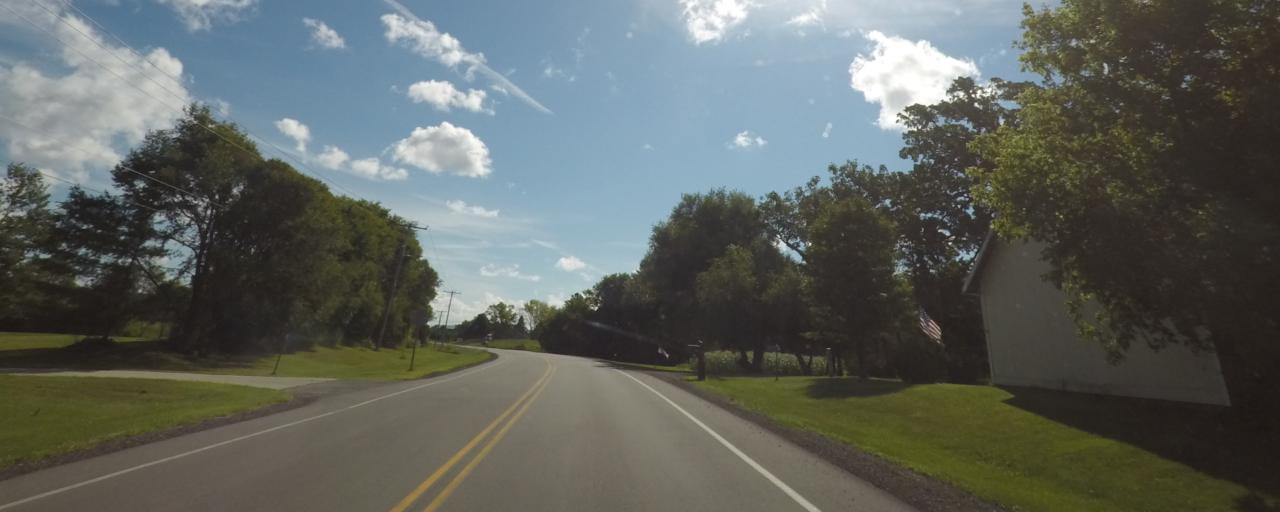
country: US
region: Wisconsin
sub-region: Waukesha County
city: Oconomowoc
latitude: 43.0748
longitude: -88.5525
